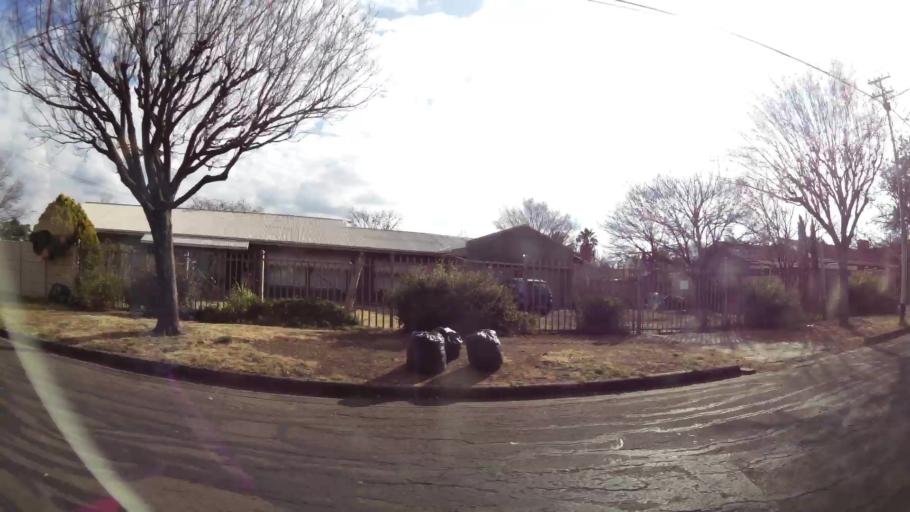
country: ZA
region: Orange Free State
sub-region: Mangaung Metropolitan Municipality
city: Bloemfontein
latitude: -29.0797
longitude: 26.2170
